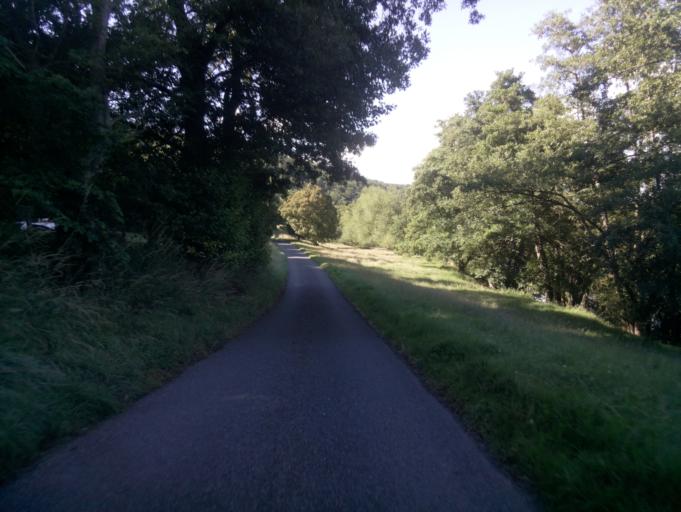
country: GB
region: England
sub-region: Herefordshire
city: Yatton
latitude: 51.9649
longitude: -2.5592
